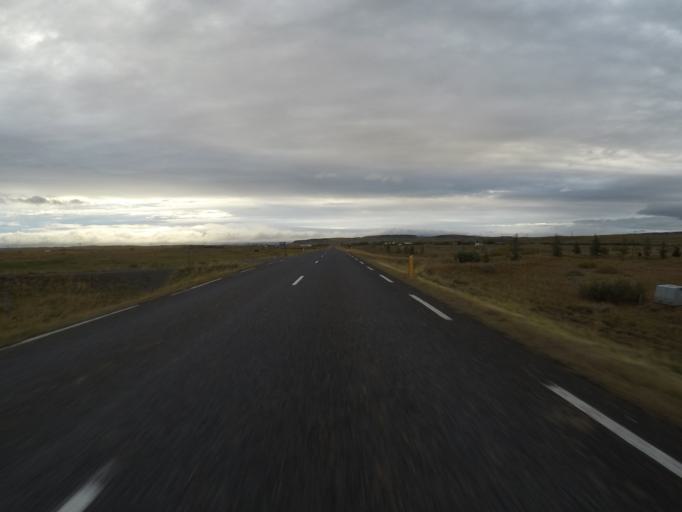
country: IS
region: South
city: Vestmannaeyjar
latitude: 64.0411
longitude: -20.2268
